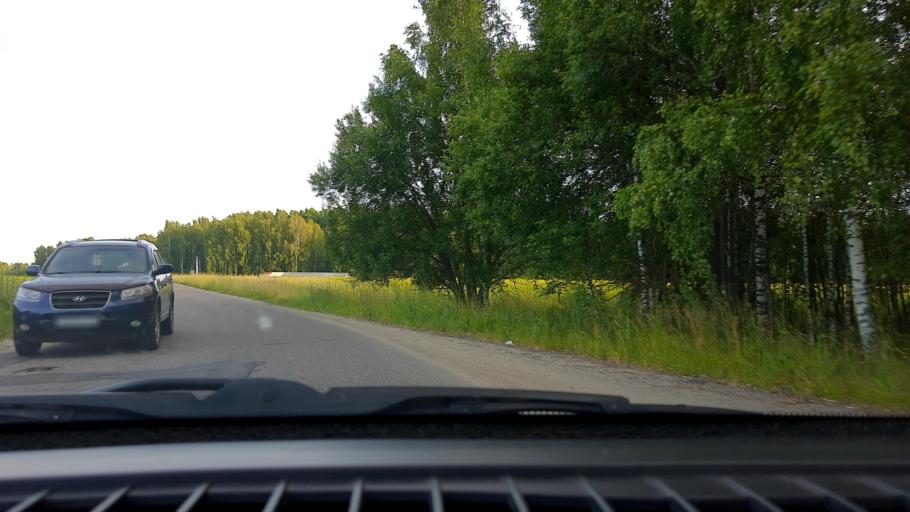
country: RU
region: Nizjnij Novgorod
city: Kstovo
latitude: 56.2717
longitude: 44.3272
